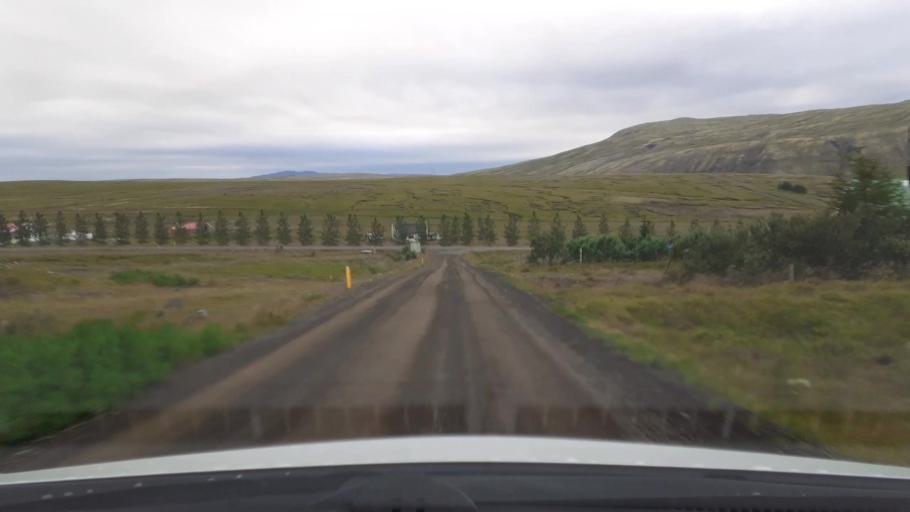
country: IS
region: Capital Region
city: Mosfellsbaer
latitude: 64.1902
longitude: -21.5383
